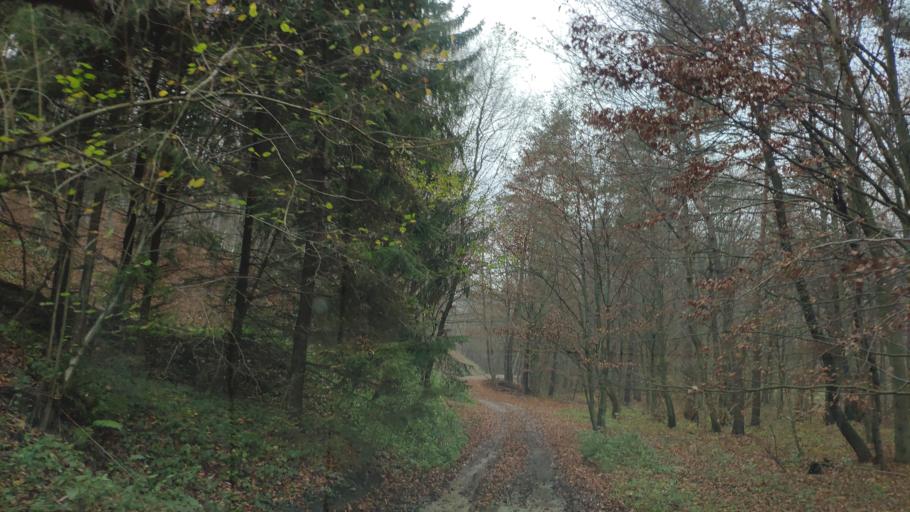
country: SK
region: Presovsky
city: Sabinov
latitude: 49.1452
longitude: 21.2133
